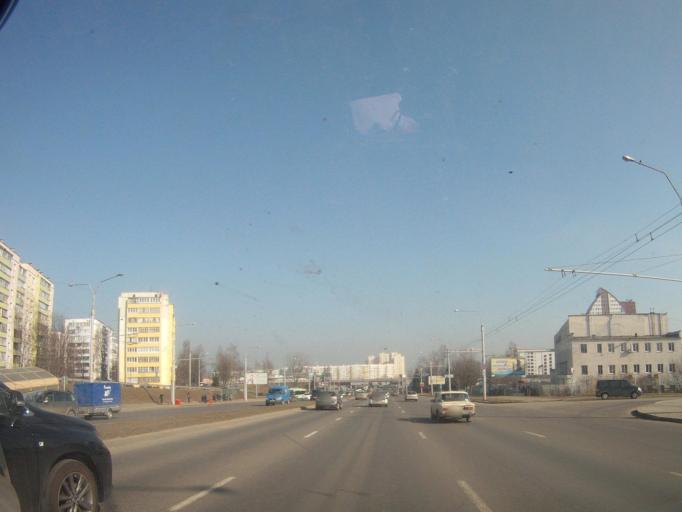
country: BY
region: Minsk
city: Novoye Medvezhino
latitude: 53.9238
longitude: 27.5025
